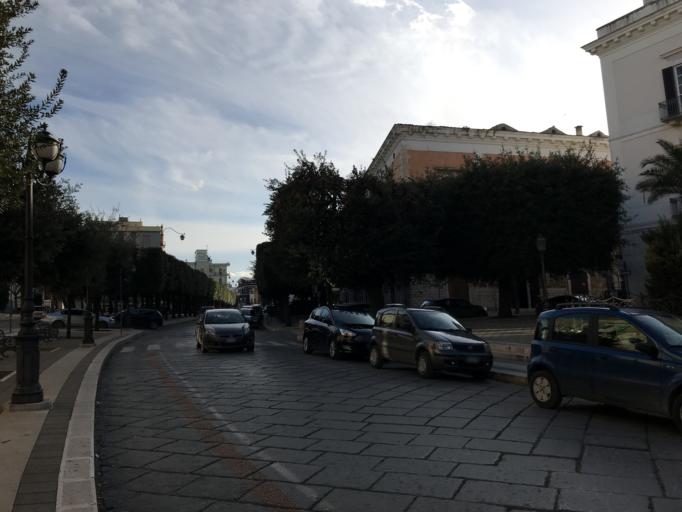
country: IT
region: Apulia
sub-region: Provincia di Bari
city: Corato
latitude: 41.1525
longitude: 16.4133
